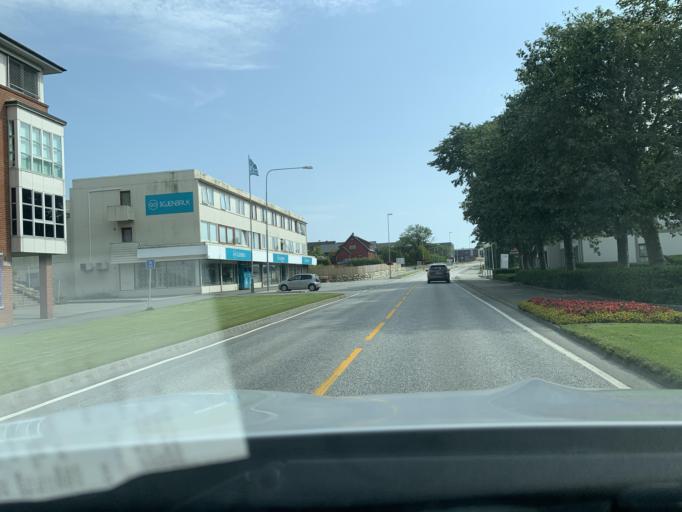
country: NO
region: Rogaland
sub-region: Klepp
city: Kleppe
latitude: 58.7733
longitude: 5.6295
